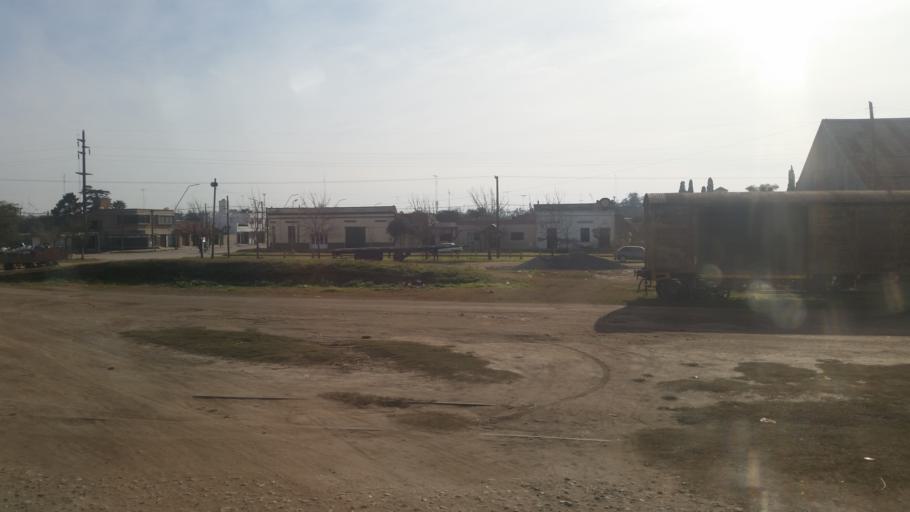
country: AR
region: Cordoba
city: Morrison
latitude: -32.5950
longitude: -62.8352
